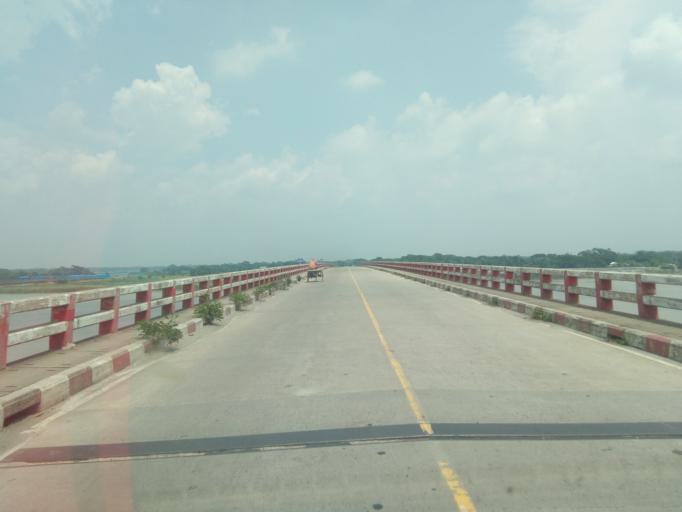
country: BD
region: Dhaka
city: Char Bhadrasan
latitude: 23.3786
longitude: 90.1154
